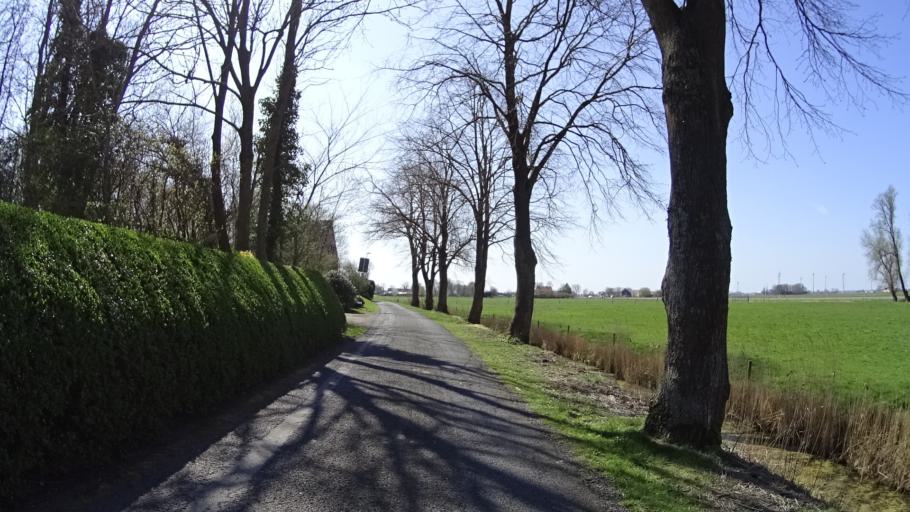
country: DE
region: Lower Saxony
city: Leer
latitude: 53.2067
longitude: 7.4043
